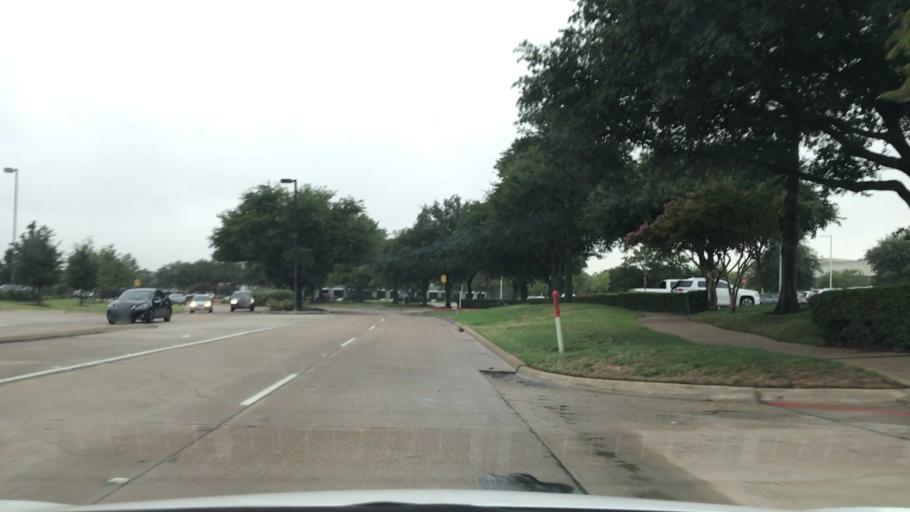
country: US
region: Texas
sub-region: Dallas County
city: Coppell
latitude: 32.9329
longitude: -97.0116
